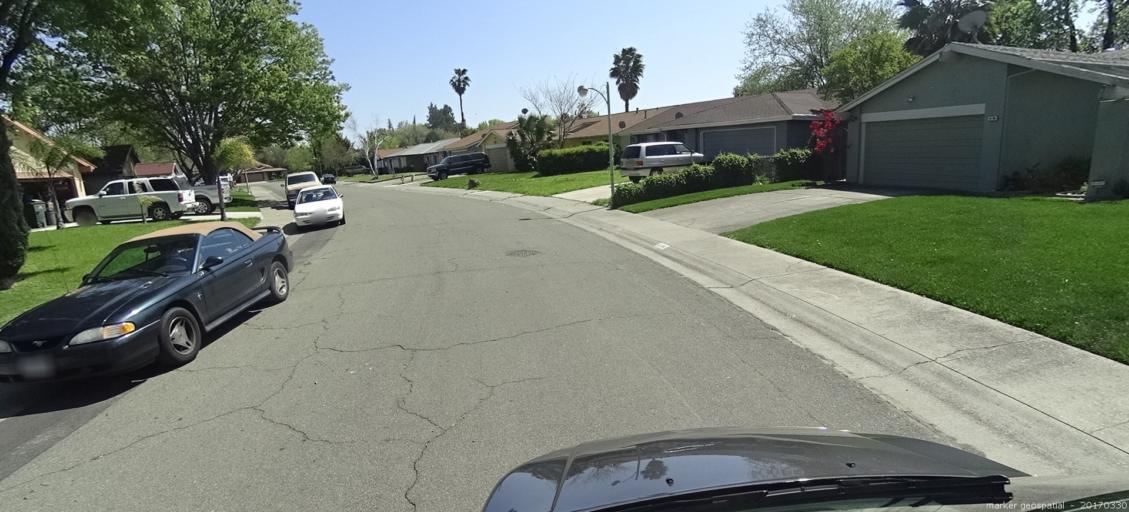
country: US
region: California
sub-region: Sacramento County
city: Florin
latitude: 38.4696
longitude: -121.4304
